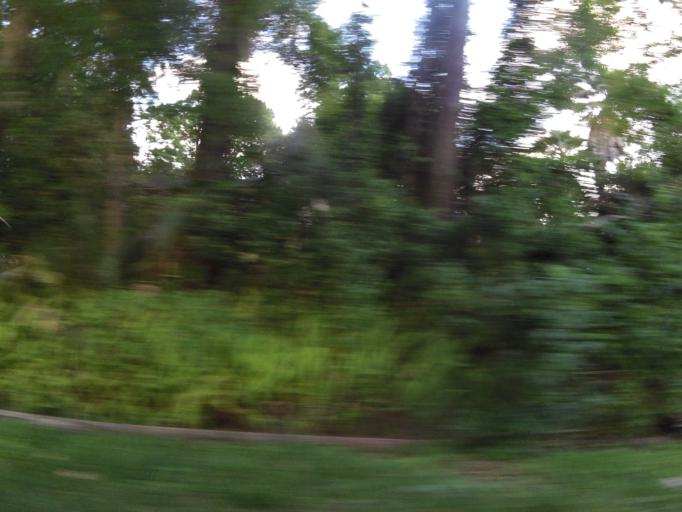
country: US
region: Florida
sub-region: Duval County
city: Jacksonville
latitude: 30.2936
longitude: -81.7389
